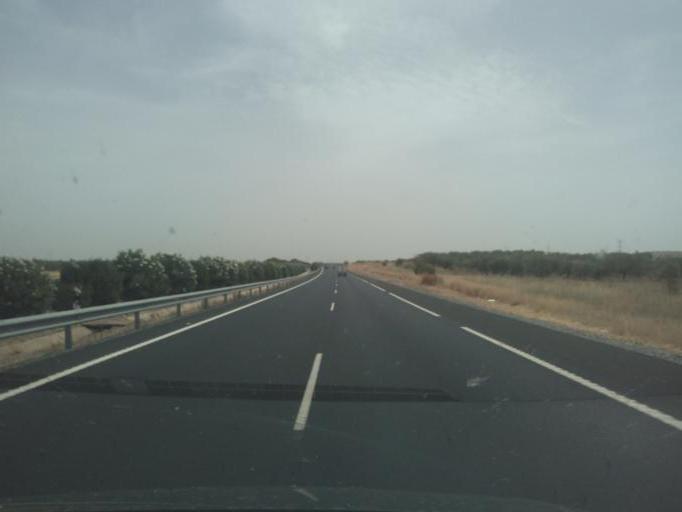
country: ES
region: Andalusia
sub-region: Provincia de Huelva
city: Bonares
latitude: 37.3403
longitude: -6.7044
